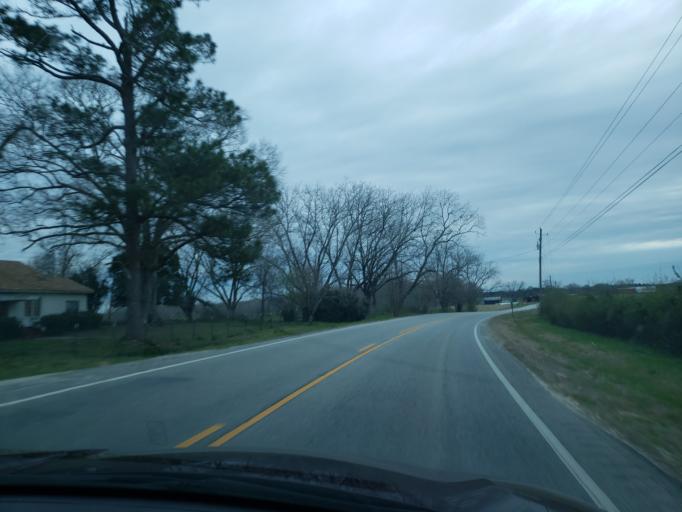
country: US
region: Alabama
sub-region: Chambers County
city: Lafayette
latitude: 32.9923
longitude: -85.3939
